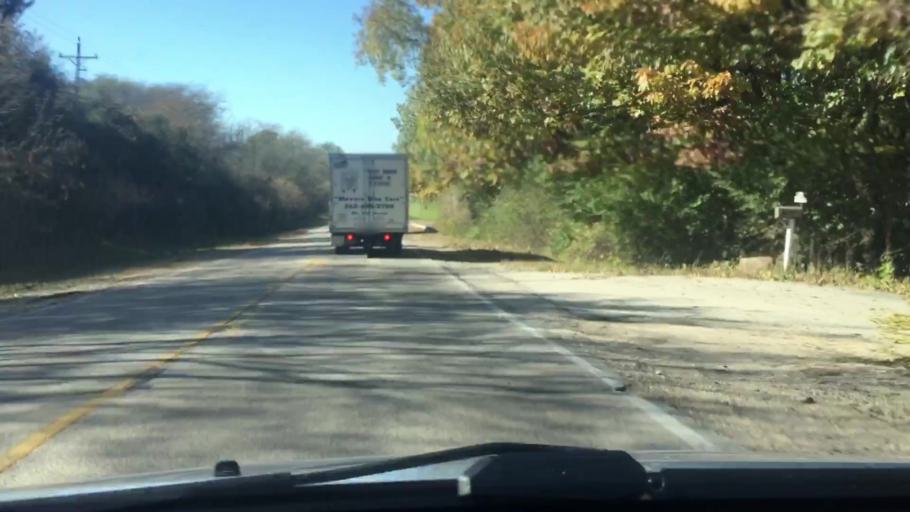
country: US
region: Wisconsin
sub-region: Waukesha County
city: Waukesha
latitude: 42.9884
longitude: -88.2974
